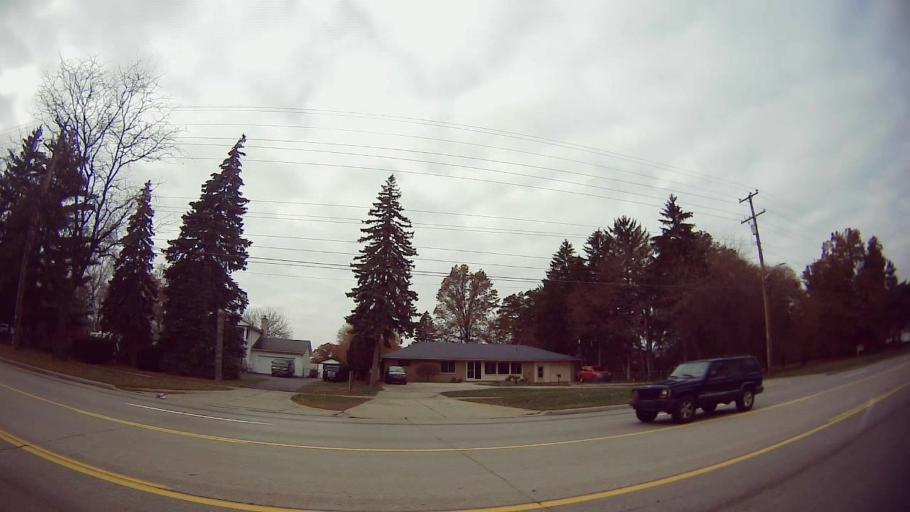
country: US
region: Michigan
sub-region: Oakland County
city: Madison Heights
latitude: 42.4990
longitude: -83.0671
